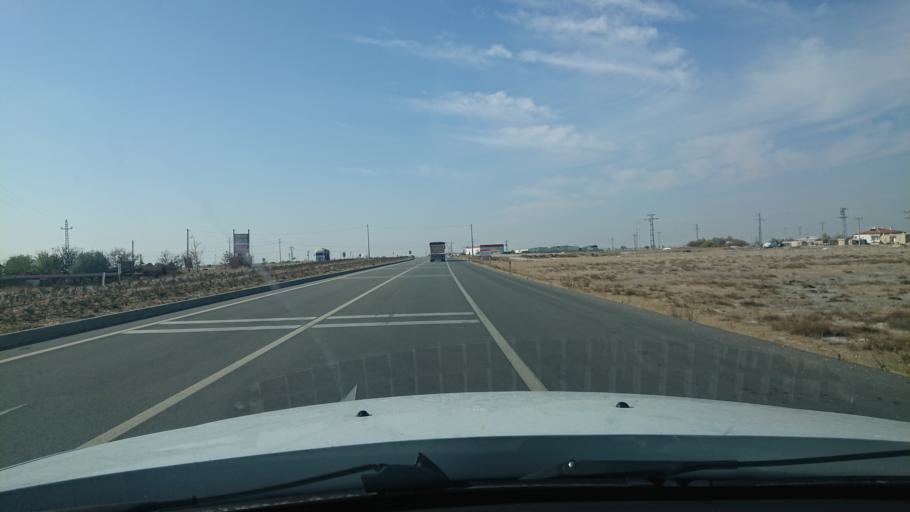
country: TR
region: Aksaray
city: Sultanhani
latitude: 38.2522
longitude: 33.4850
